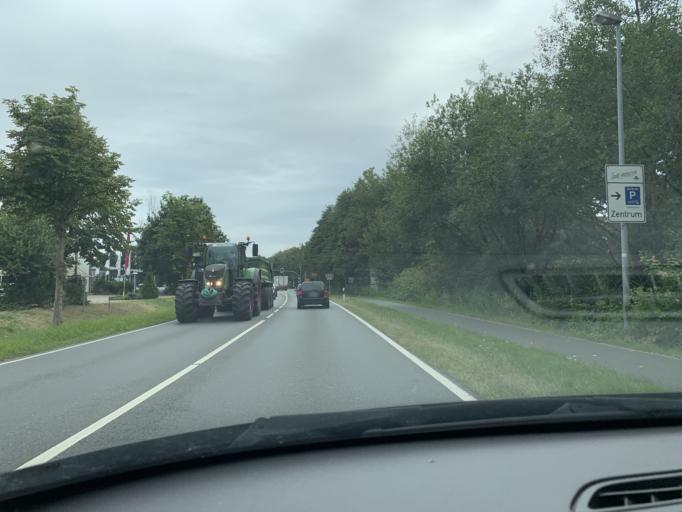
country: DE
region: Lower Saxony
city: Westerstede
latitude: 53.2584
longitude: 7.9363
